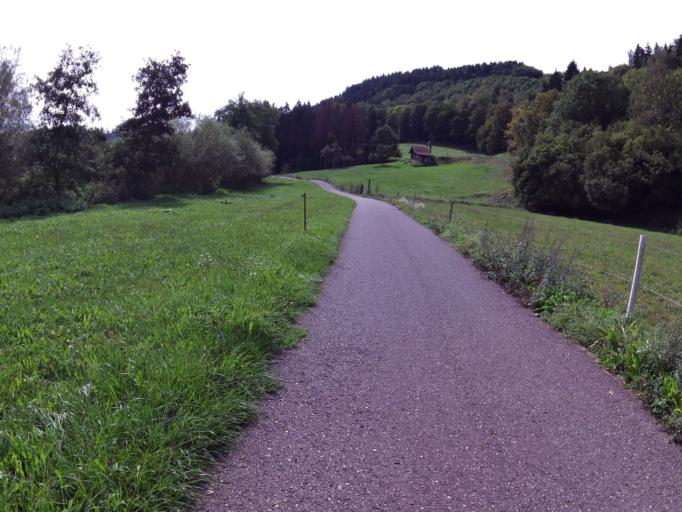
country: DE
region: Baden-Wuerttemberg
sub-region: Freiburg Region
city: Sulz am Neckar
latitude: 48.4035
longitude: 8.6396
